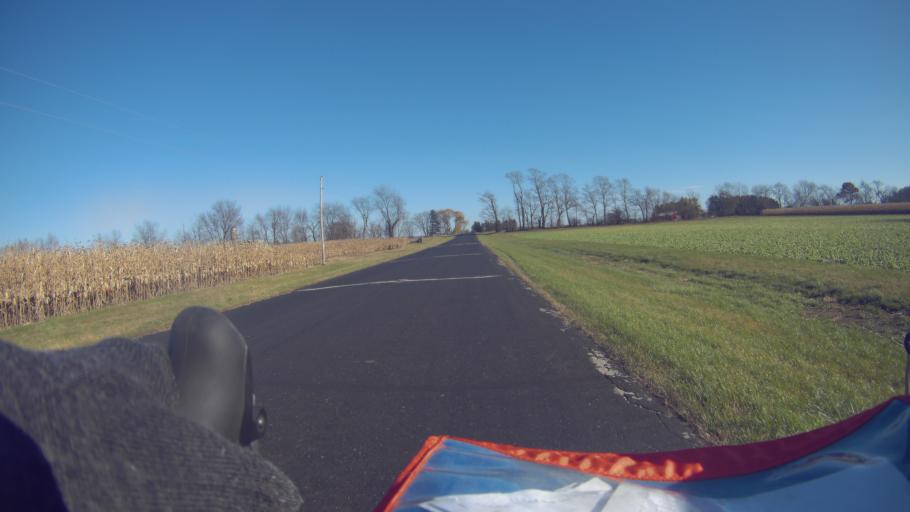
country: US
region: Wisconsin
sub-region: Dane County
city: Stoughton
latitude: 42.8463
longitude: -89.2076
